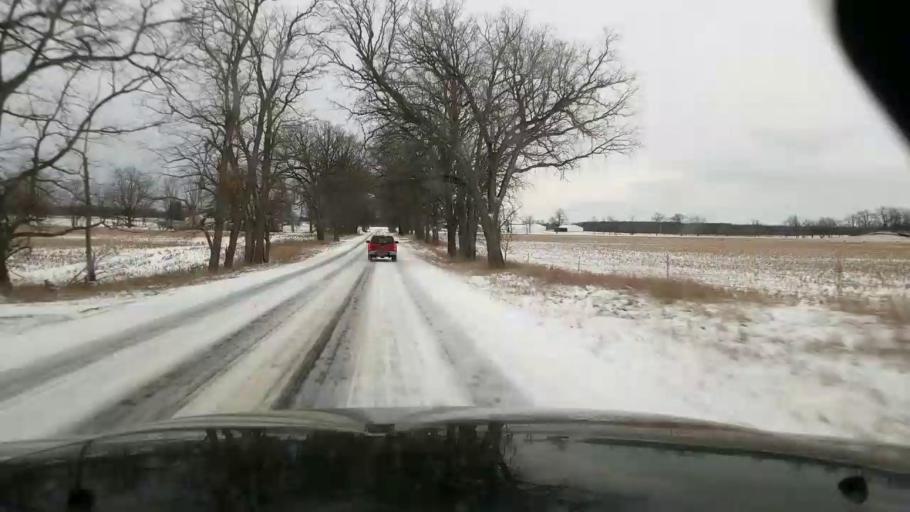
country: US
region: Michigan
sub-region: Jackson County
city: Spring Arbor
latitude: 42.1729
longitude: -84.5005
